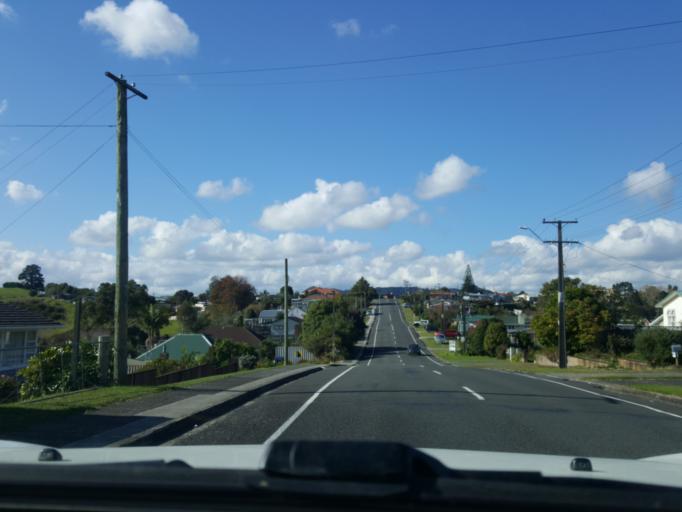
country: NZ
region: Waikato
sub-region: Waikato District
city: Ngaruawahia
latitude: -37.5479
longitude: 175.1642
